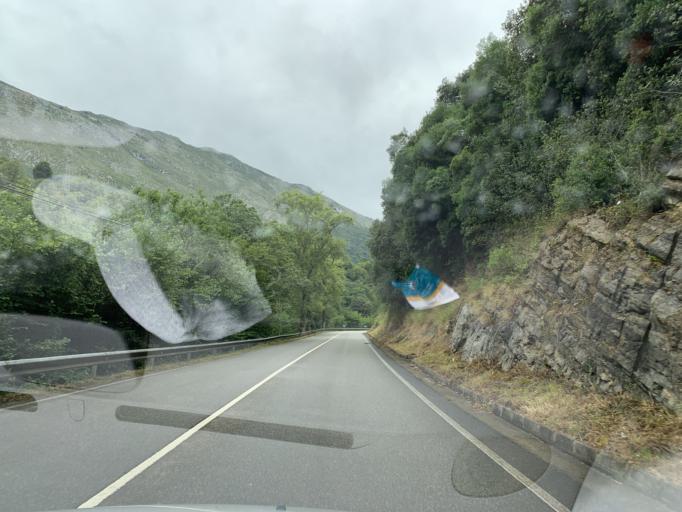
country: ES
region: Cantabria
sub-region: Provincia de Cantabria
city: Tresviso
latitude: 43.3180
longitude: -4.6145
